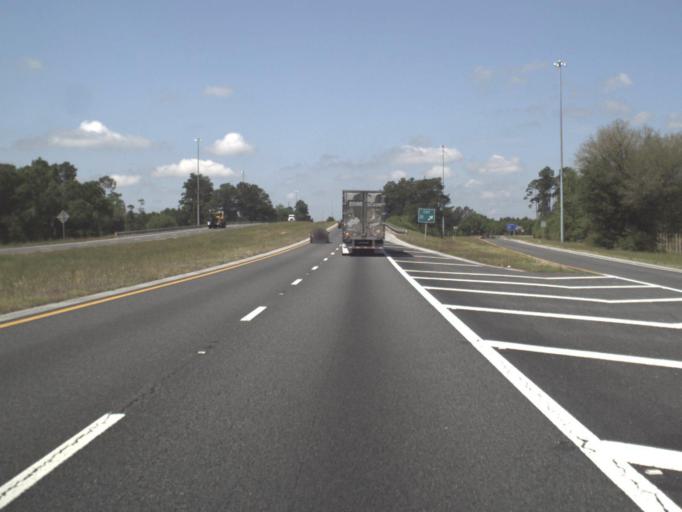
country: US
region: Florida
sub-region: Santa Rosa County
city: East Milton
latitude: 30.6205
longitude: -86.9584
